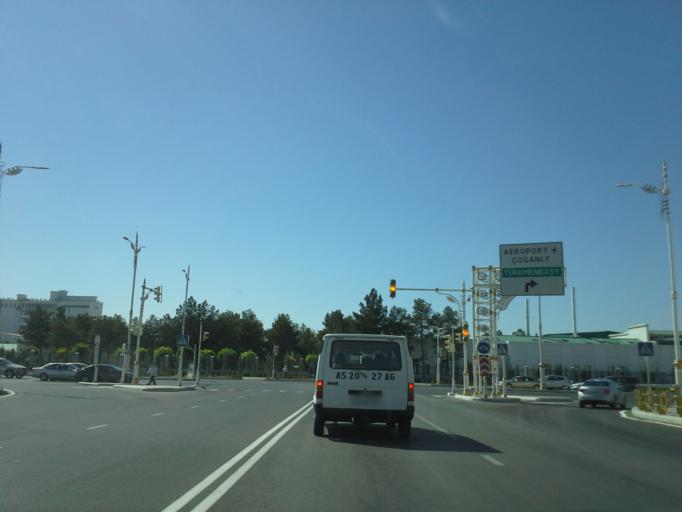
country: TM
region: Ahal
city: Ashgabat
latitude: 37.9578
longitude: 58.3776
